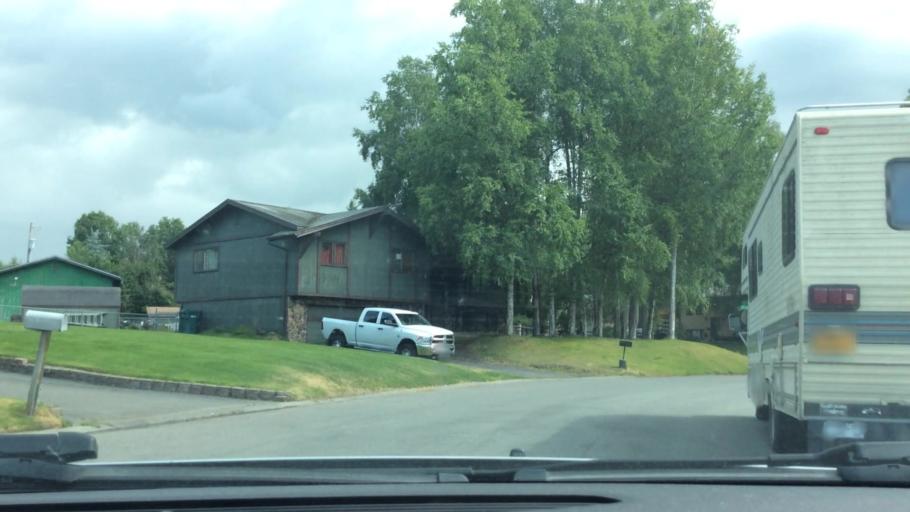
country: US
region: Alaska
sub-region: Anchorage Municipality
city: Elmendorf Air Force Base
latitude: 61.2218
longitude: -149.7531
